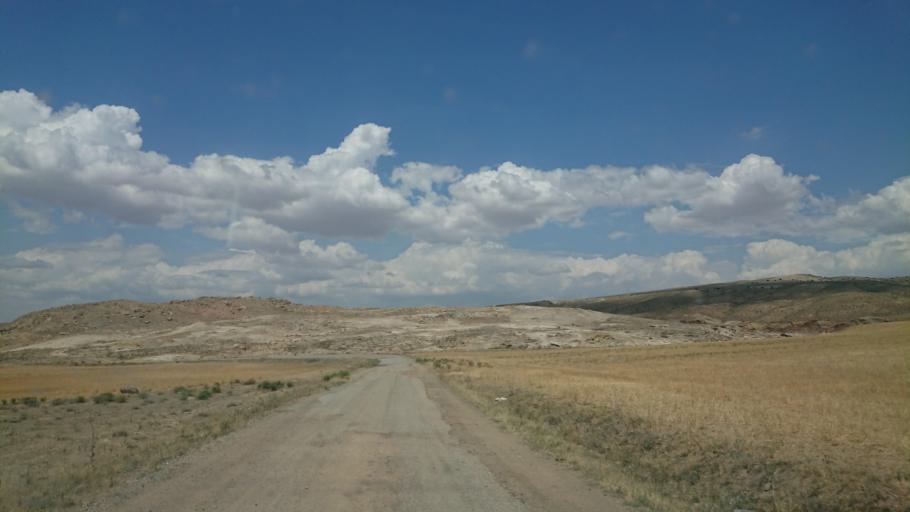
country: TR
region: Aksaray
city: Sariyahsi
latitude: 38.9954
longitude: 33.9143
